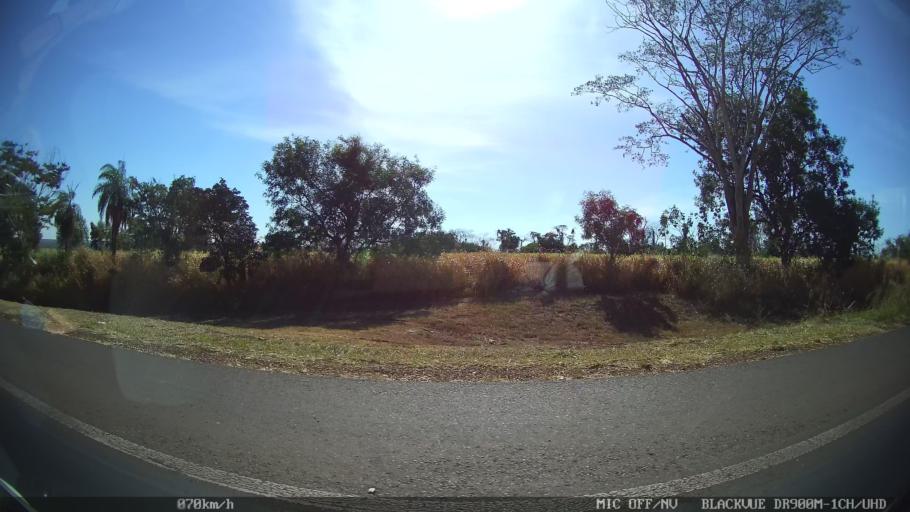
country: BR
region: Sao Paulo
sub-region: Barretos
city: Barretos
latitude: -20.5756
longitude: -48.6801
